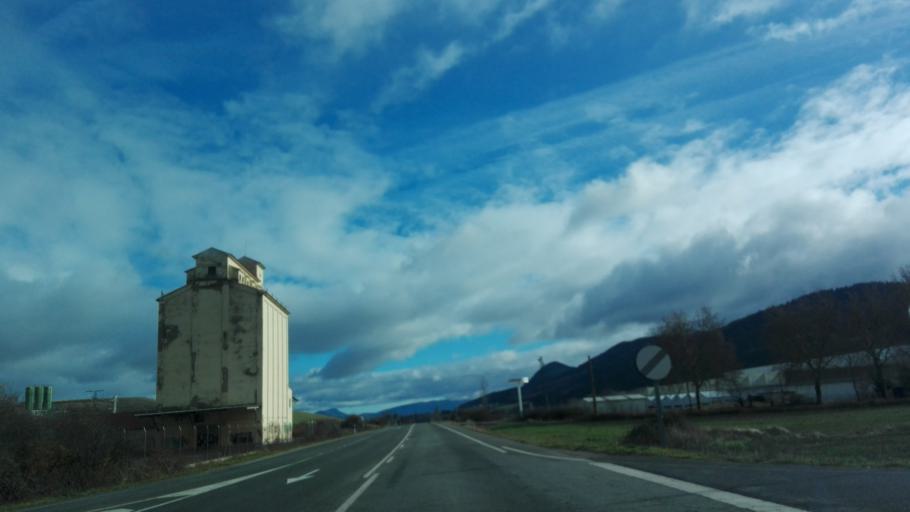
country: ES
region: Navarre
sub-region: Provincia de Navarra
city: Lizoain
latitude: 42.7791
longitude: -1.4525
